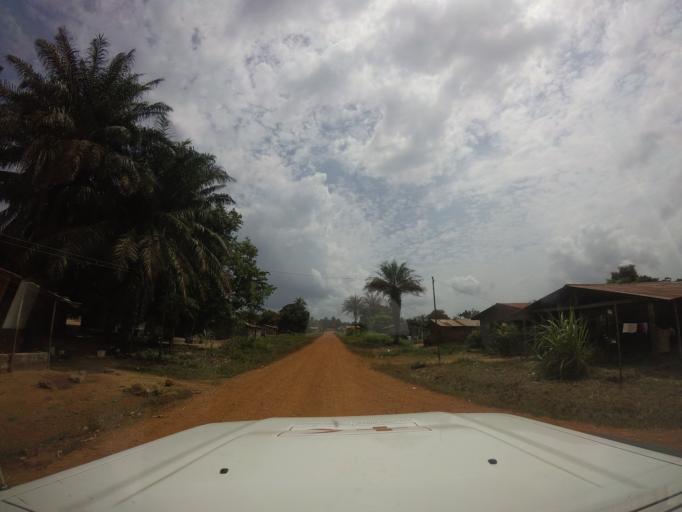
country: LR
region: Grand Cape Mount
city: Robertsport
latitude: 6.7557
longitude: -11.3733
